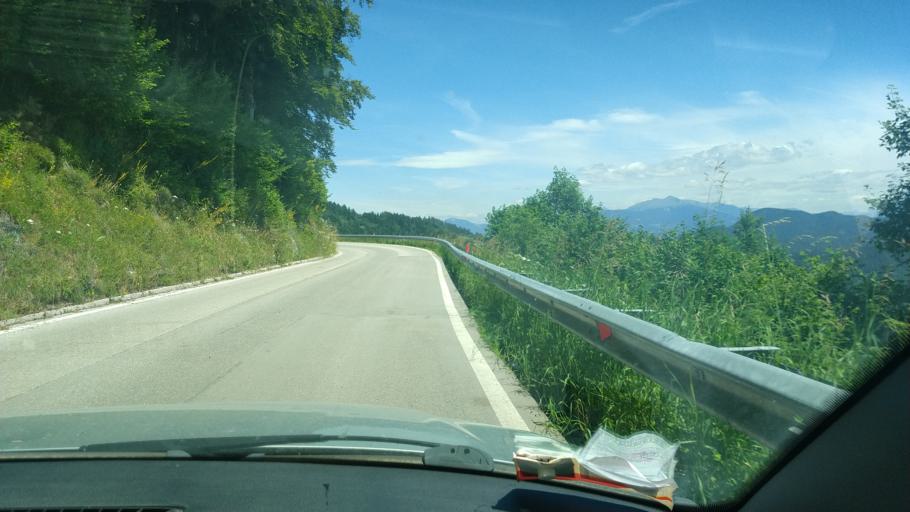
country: IT
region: Trentino-Alto Adige
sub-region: Provincia di Trento
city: Folgaria
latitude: 45.9160
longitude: 11.2115
